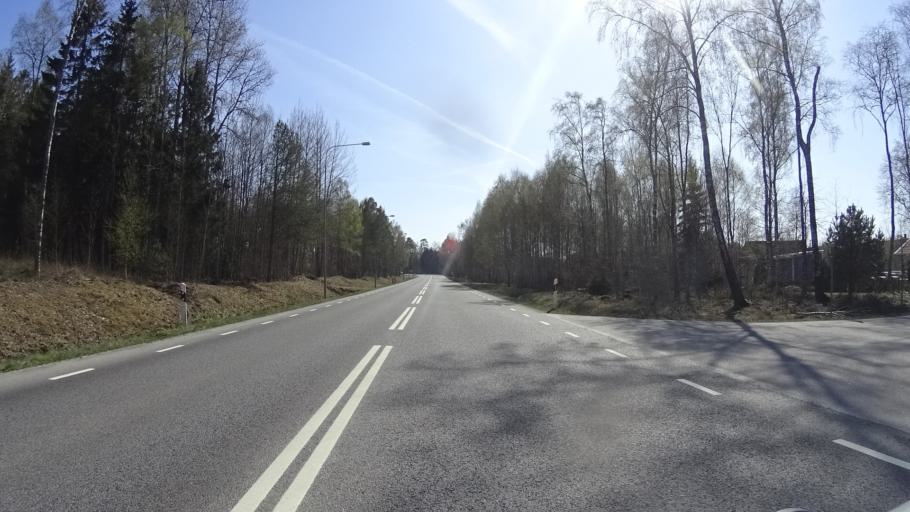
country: SE
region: Kronoberg
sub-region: Ljungby Kommun
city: Ljungby
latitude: 56.8388
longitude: 13.9734
